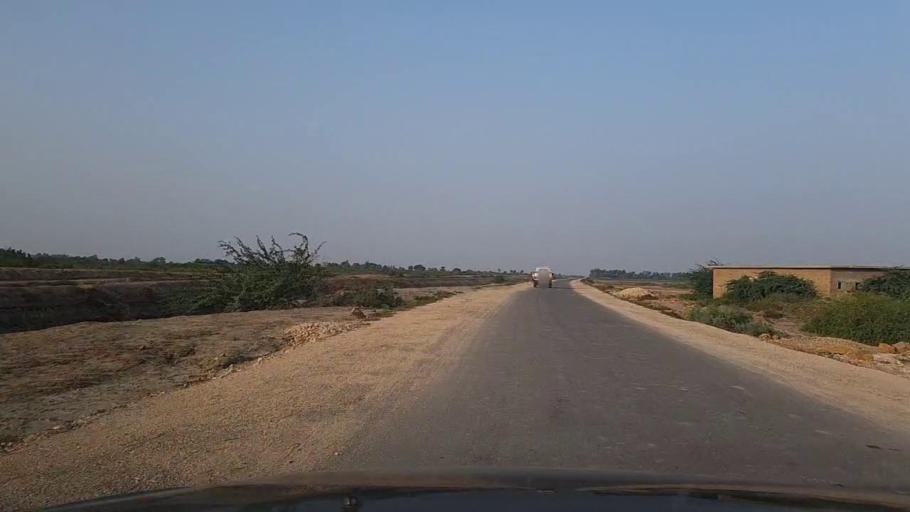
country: PK
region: Sindh
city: Mirpur Sakro
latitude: 24.4469
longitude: 67.7891
